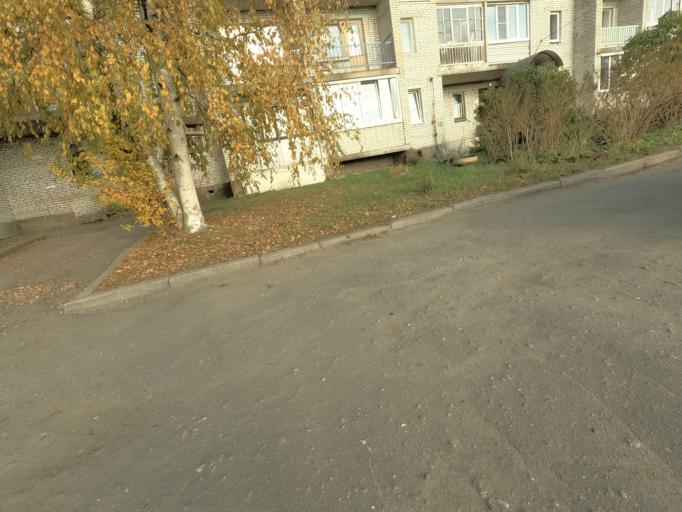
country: RU
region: Leningrad
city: Mga
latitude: 59.7460
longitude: 31.0642
